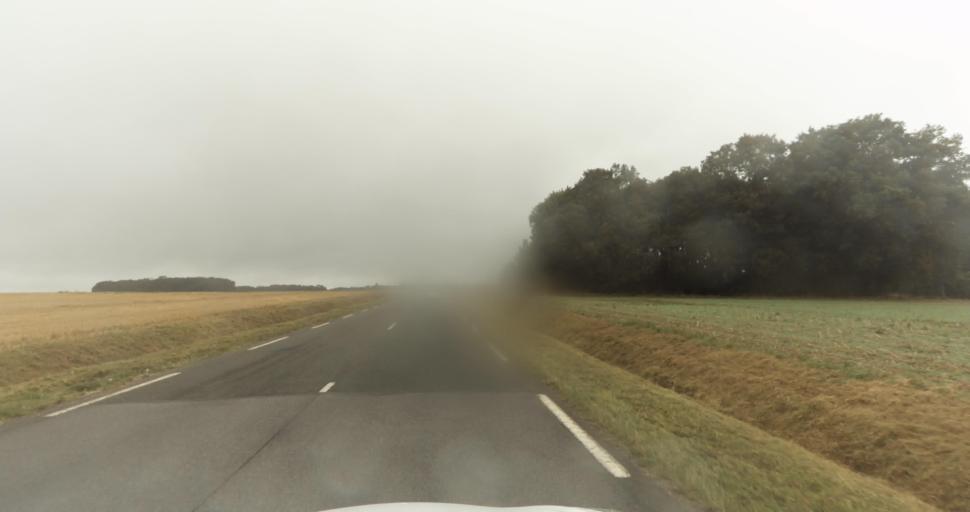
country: FR
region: Haute-Normandie
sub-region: Departement de l'Eure
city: Normanville
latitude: 49.1020
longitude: 1.1726
